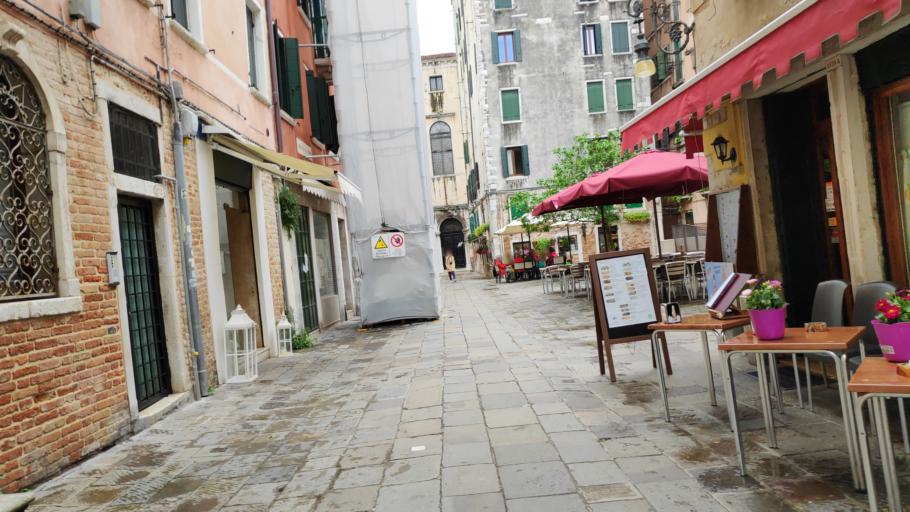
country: IT
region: Veneto
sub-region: Provincia di Venezia
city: Venice
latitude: 45.4451
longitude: 12.3260
